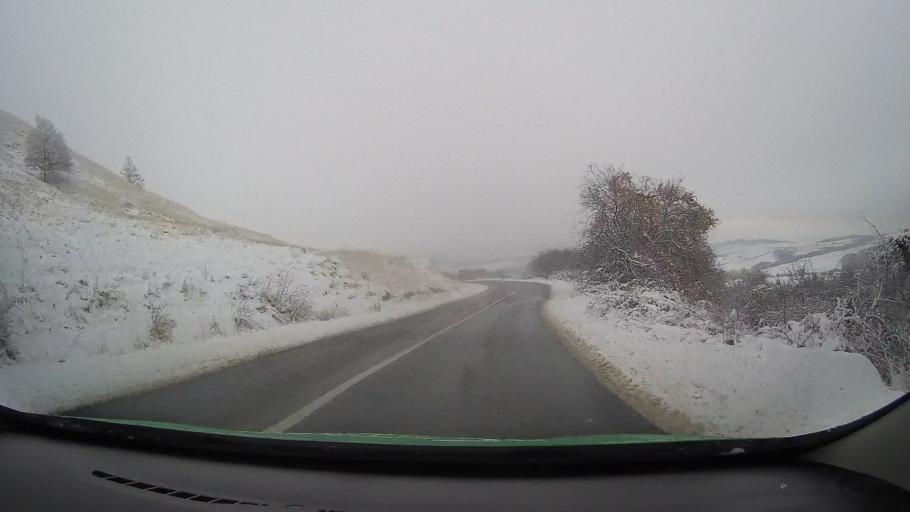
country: RO
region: Hunedoara
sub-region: Comuna Unirea
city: Unirea
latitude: 45.6603
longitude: 22.9145
